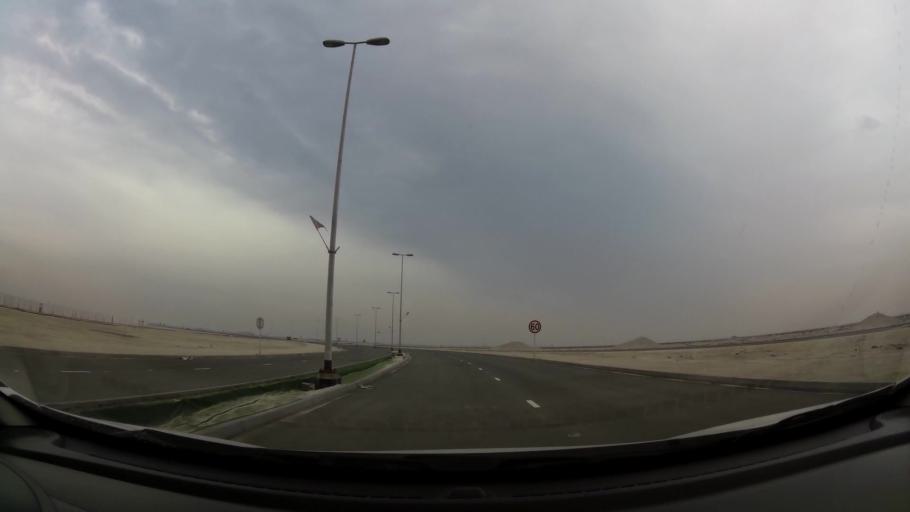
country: BH
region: Central Governorate
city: Dar Kulayb
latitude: 25.8668
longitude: 50.6055
